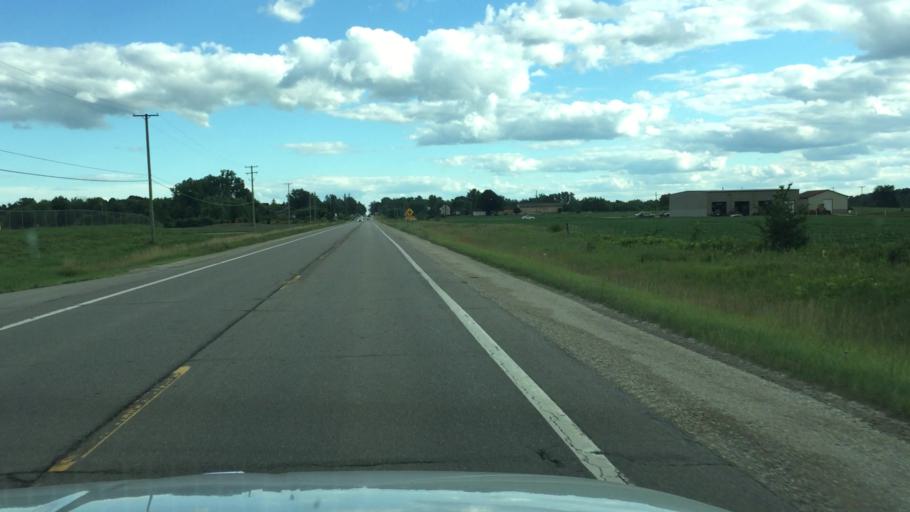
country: US
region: Michigan
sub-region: Saint Clair County
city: Yale
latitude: 43.1476
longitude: -82.7996
